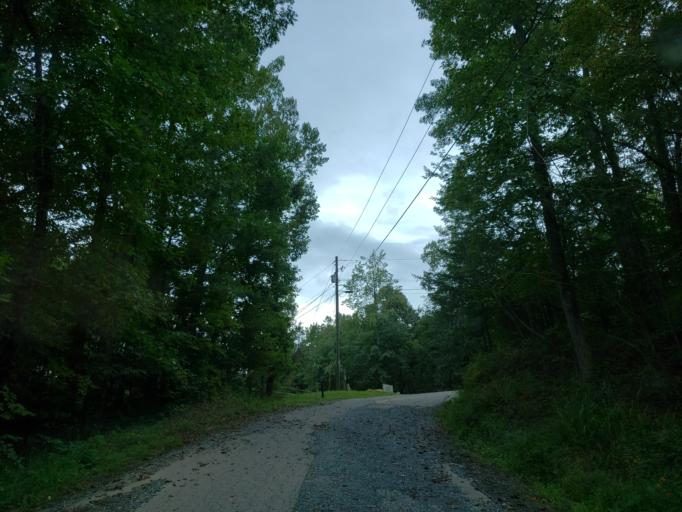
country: US
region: Georgia
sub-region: Pickens County
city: Jasper
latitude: 34.5509
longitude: -84.5155
